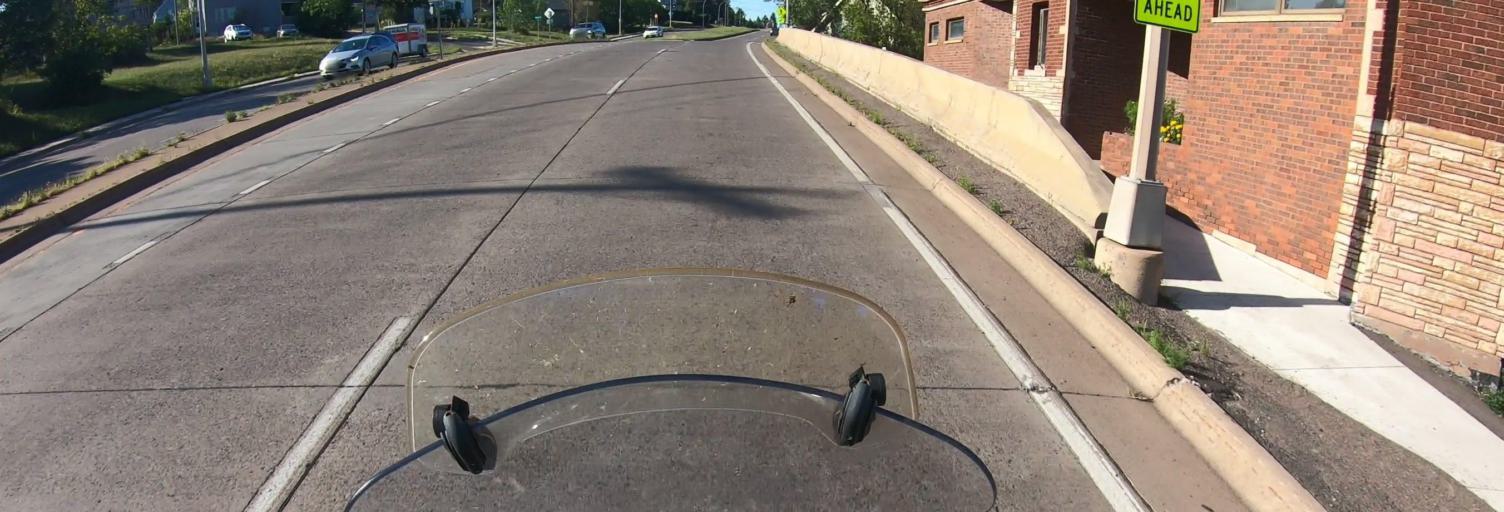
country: US
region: Minnesota
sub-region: Saint Louis County
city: Duluth
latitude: 46.7924
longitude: -92.1078
